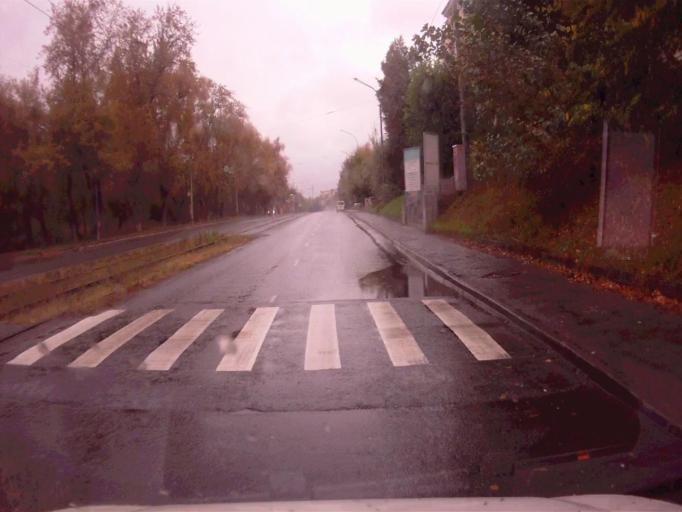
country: RU
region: Chelyabinsk
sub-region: Gorod Chelyabinsk
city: Chelyabinsk
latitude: 55.1808
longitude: 61.4147
